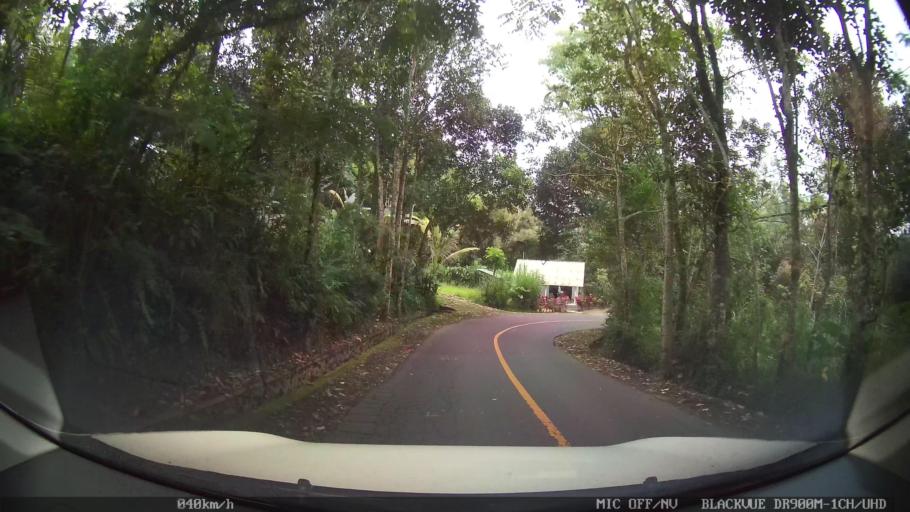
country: ID
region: Bali
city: Banjar Bias
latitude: -8.3727
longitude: 115.4339
